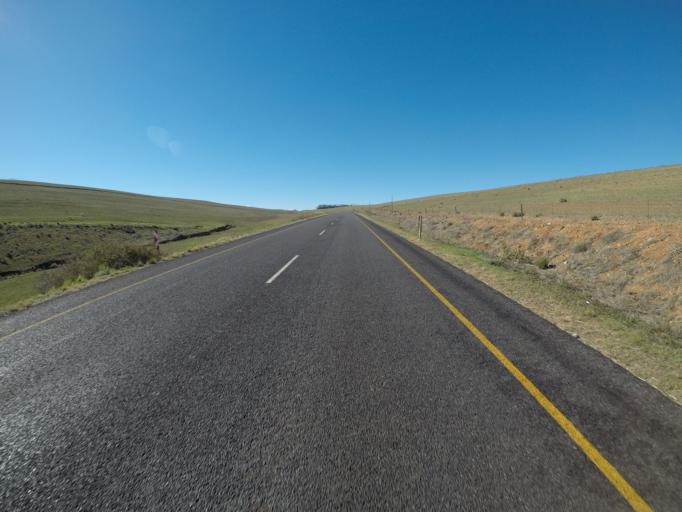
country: ZA
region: Western Cape
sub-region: Overberg District Municipality
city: Caledon
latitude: -34.1457
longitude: 19.4934
